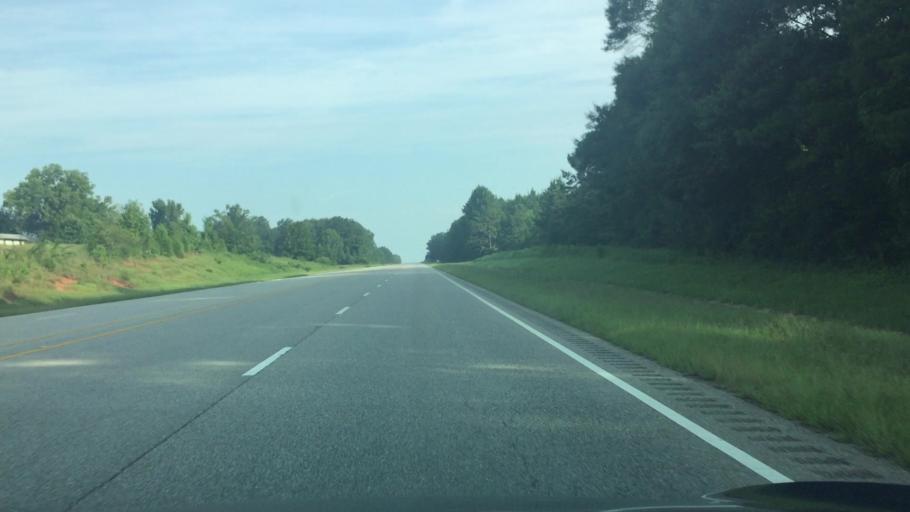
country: US
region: Alabama
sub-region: Butler County
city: Georgiana
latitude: 31.4710
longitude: -86.6670
